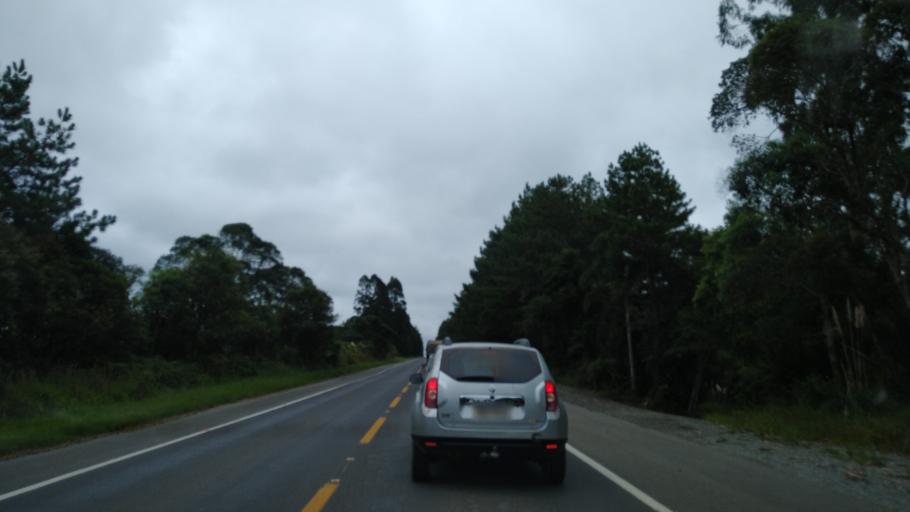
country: BR
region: Santa Catarina
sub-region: Tres Barras
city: Tres Barras
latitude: -26.1826
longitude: -50.2143
